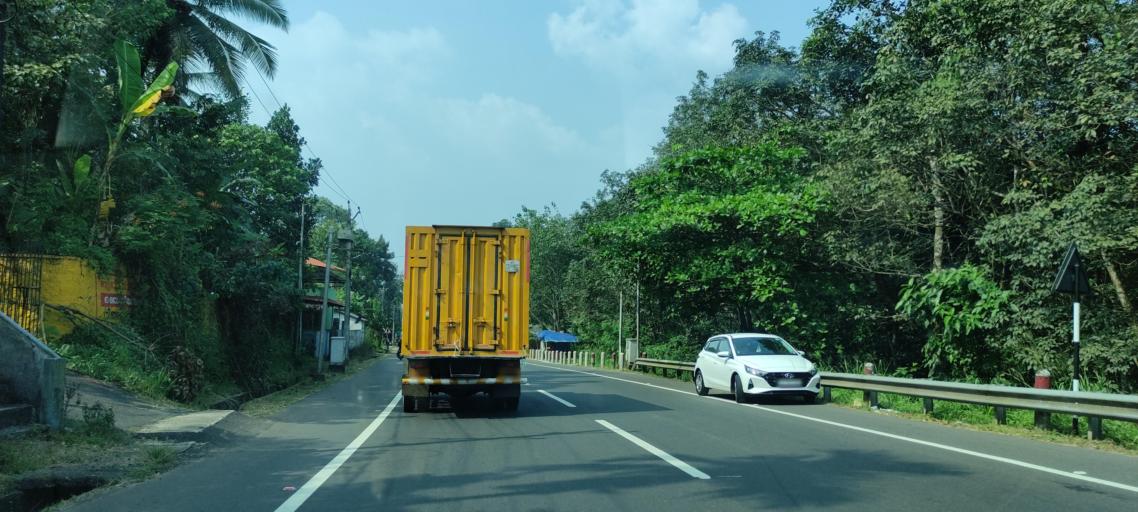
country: IN
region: Kerala
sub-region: Alappuzha
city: Chengannur
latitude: 9.2860
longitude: 76.6524
